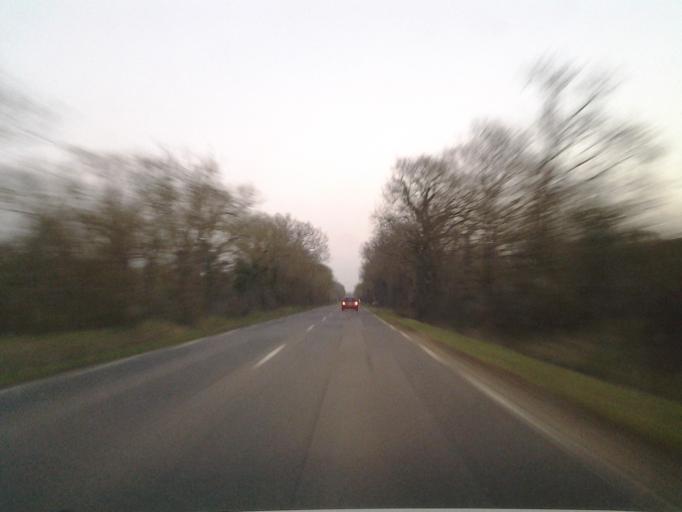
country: FR
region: Pays de la Loire
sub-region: Departement de la Vendee
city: Saint-Gervais
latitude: 46.8961
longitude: -1.9840
